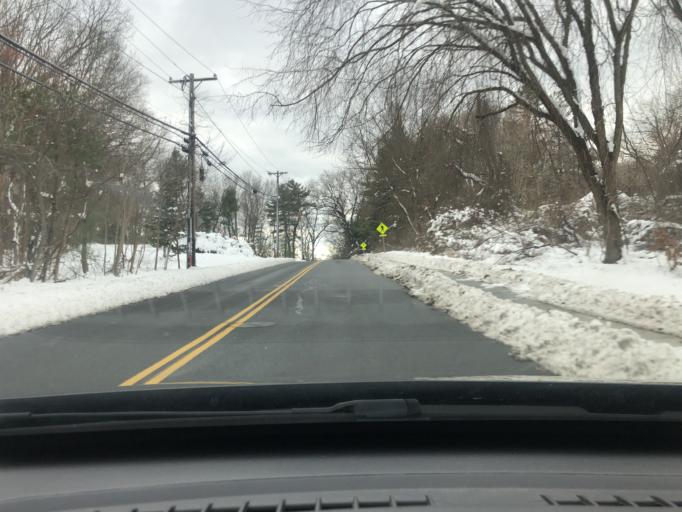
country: US
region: Massachusetts
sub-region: Middlesex County
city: Maynard
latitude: 42.4361
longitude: -71.4744
